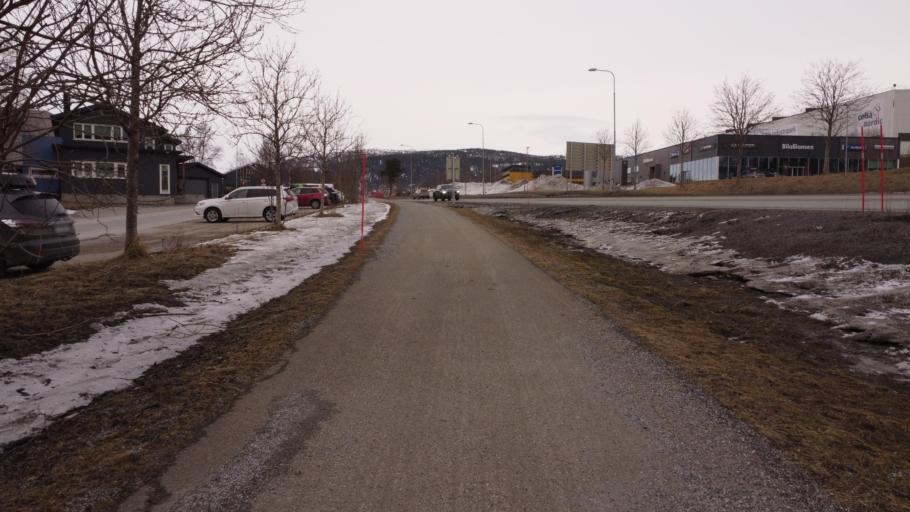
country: NO
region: Nordland
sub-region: Rana
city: Mo i Rana
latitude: 66.3099
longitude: 14.1533
